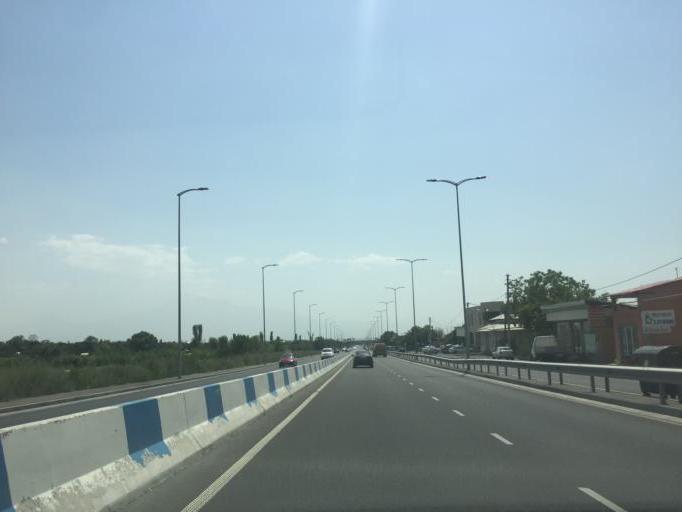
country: AM
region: Ararat
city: Norabats'
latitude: 40.1196
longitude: 44.4818
